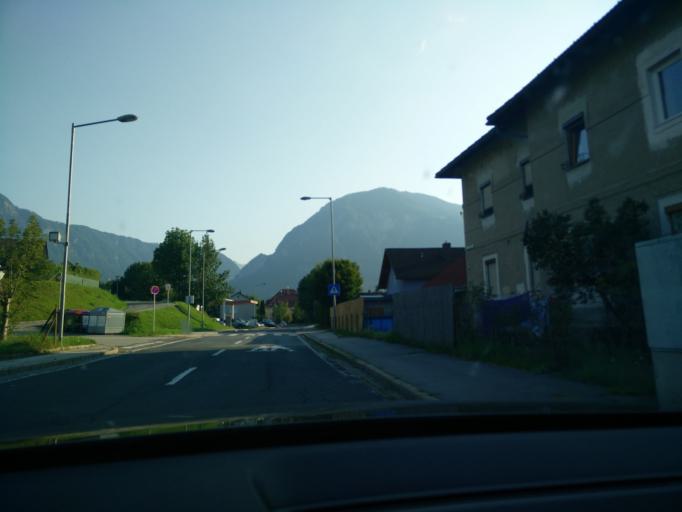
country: AT
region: Carinthia
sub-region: Politischer Bezirk Klagenfurt Land
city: Ferlach
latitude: 46.5321
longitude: 14.3036
